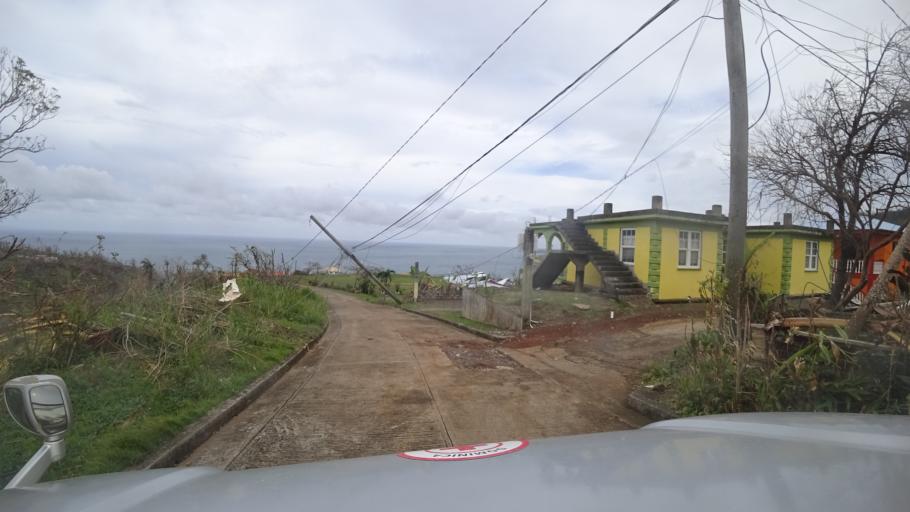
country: DM
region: Saint John
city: Portsmouth
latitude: 15.6131
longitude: -61.4117
